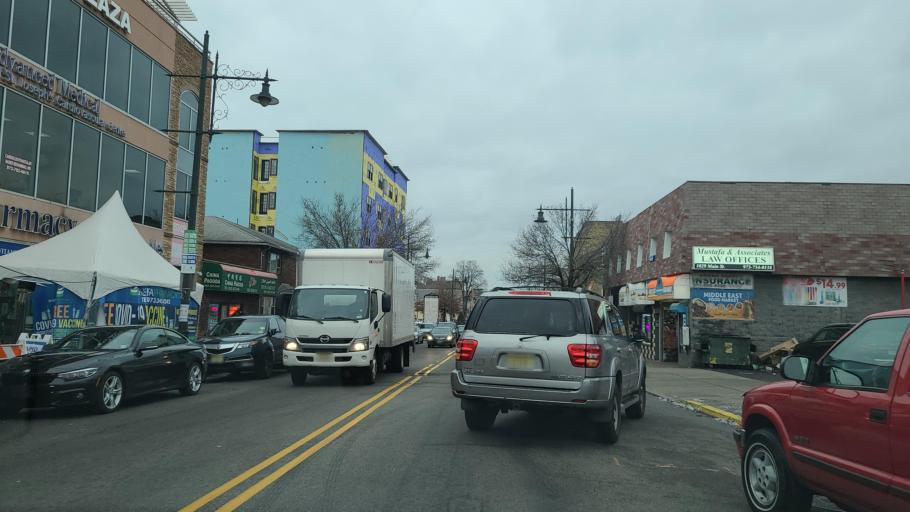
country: US
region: New Jersey
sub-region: Passaic County
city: Paterson
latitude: 40.8927
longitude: -74.1576
